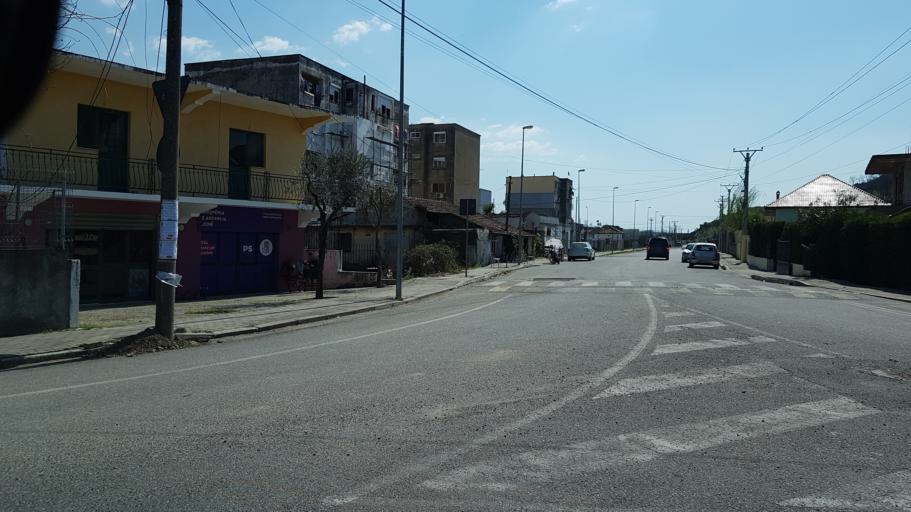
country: AL
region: Shkoder
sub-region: Rrethi i Malesia e Madhe
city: Kuc
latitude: 42.0536
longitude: 19.5224
